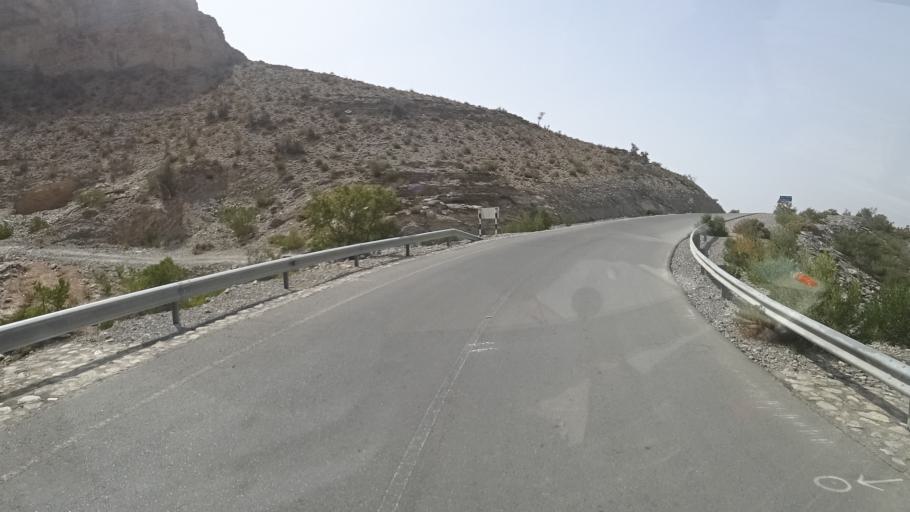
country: OM
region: Al Batinah
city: Bayt al `Awabi
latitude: 23.1629
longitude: 57.4217
